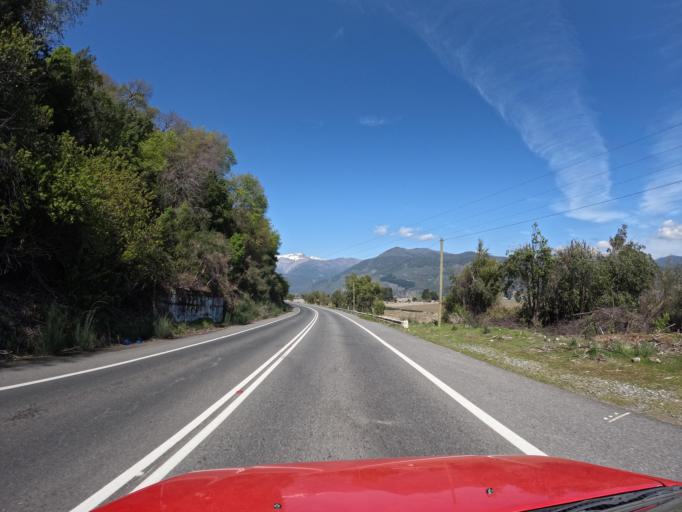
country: CL
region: Maule
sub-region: Provincia de Linares
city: Colbun
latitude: -35.6997
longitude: -71.2236
